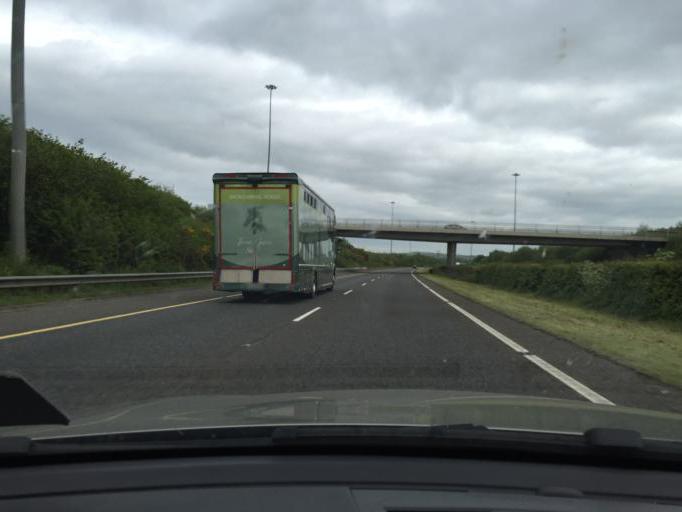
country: IE
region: Leinster
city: Balrothery
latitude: 53.5996
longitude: -6.2218
